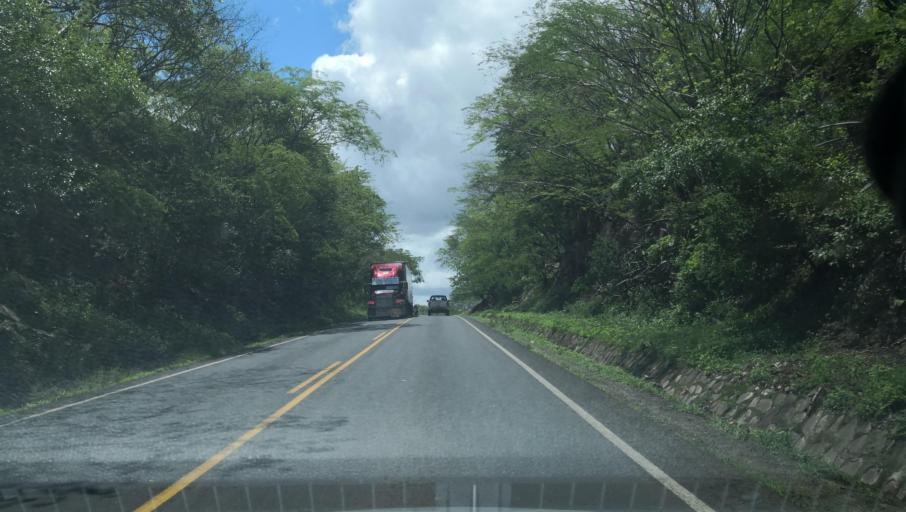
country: NI
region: Esteli
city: Condega
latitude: 13.3867
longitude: -86.4013
